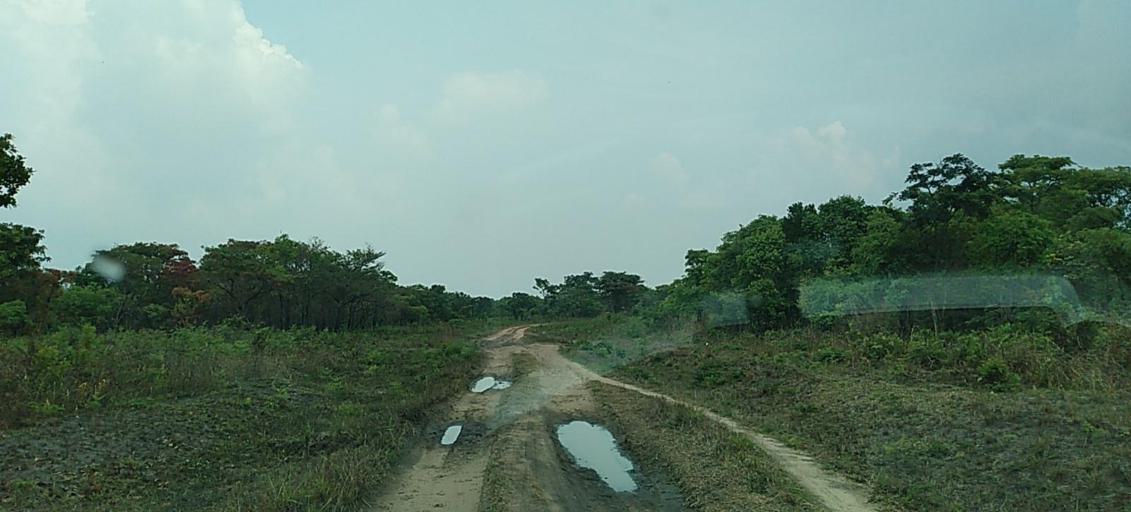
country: ZM
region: North-Western
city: Mwinilunga
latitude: -11.4300
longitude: 24.5918
